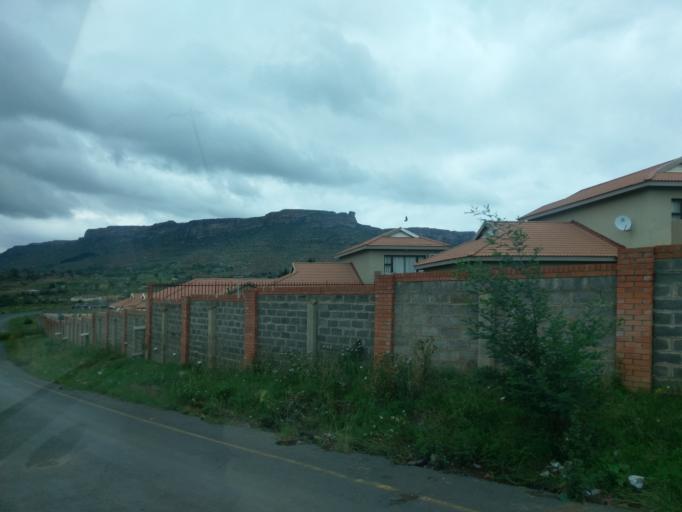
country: LS
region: Maseru
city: Maseru
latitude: -29.3949
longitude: 27.4749
